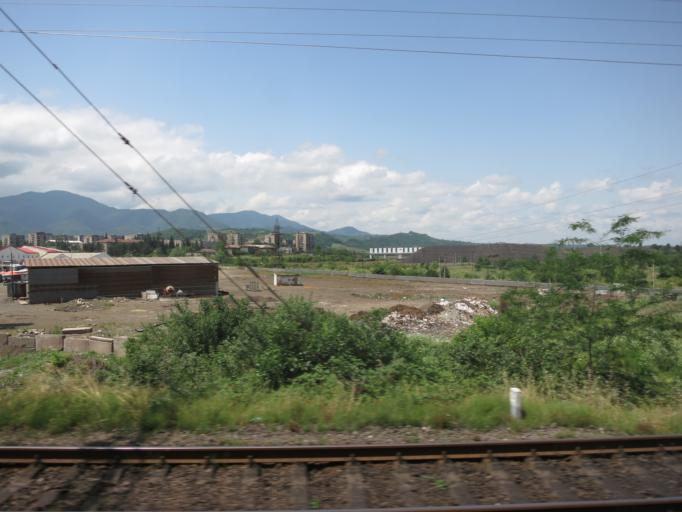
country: GE
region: Imereti
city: Zestap'oni
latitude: 42.1129
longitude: 43.0222
